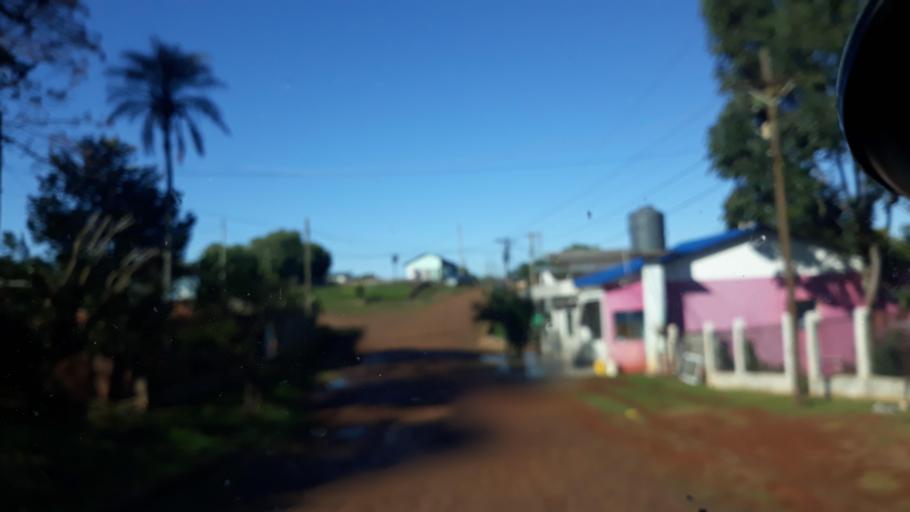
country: AR
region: Misiones
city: Bernardo de Irigoyen
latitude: -26.2564
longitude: -53.6487
